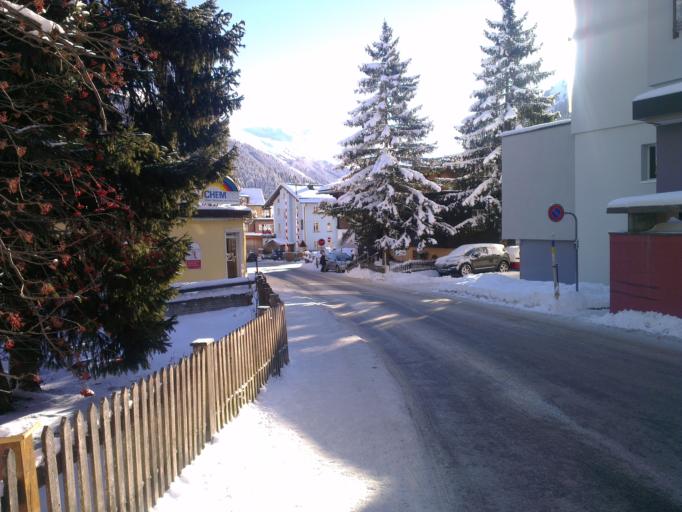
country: CH
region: Grisons
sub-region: Praettigau/Davos District
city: Davos
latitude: 46.8063
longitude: 9.8375
